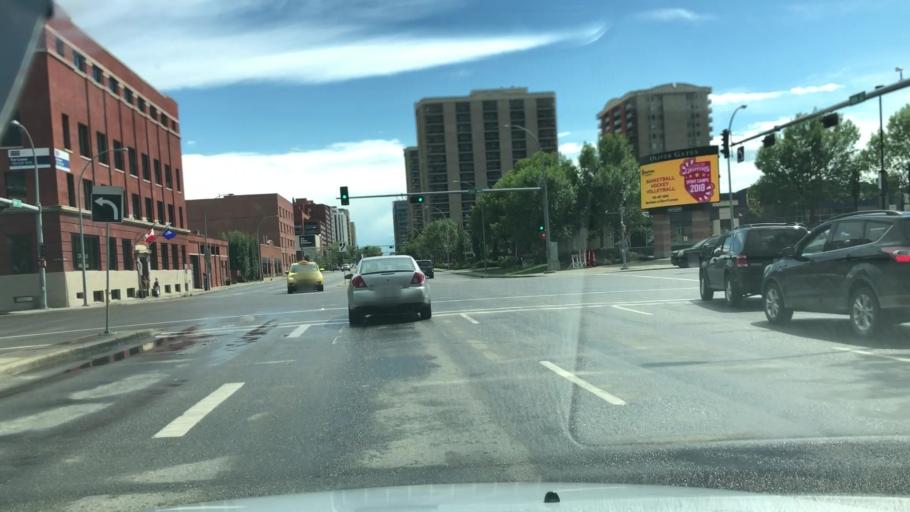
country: CA
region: Alberta
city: Edmonton
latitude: 53.5466
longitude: -113.5086
